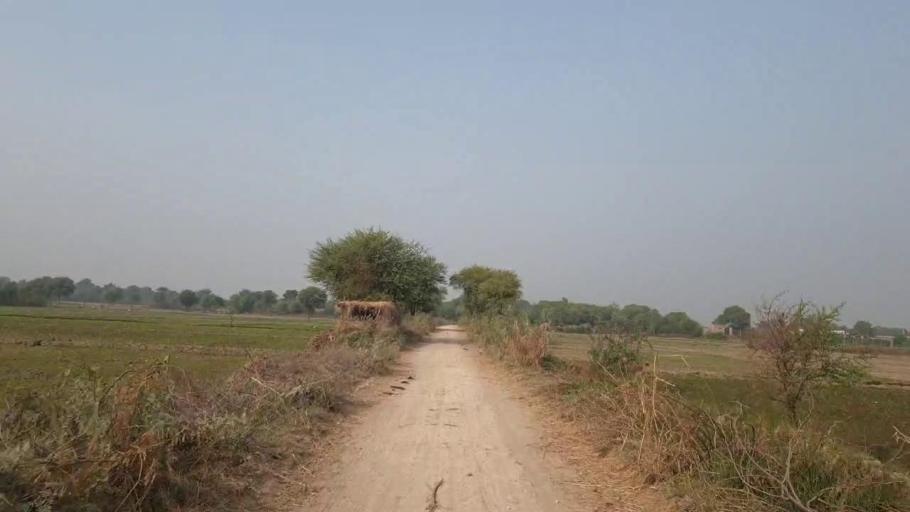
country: PK
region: Sindh
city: Tando Muhammad Khan
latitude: 25.1396
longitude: 68.6078
